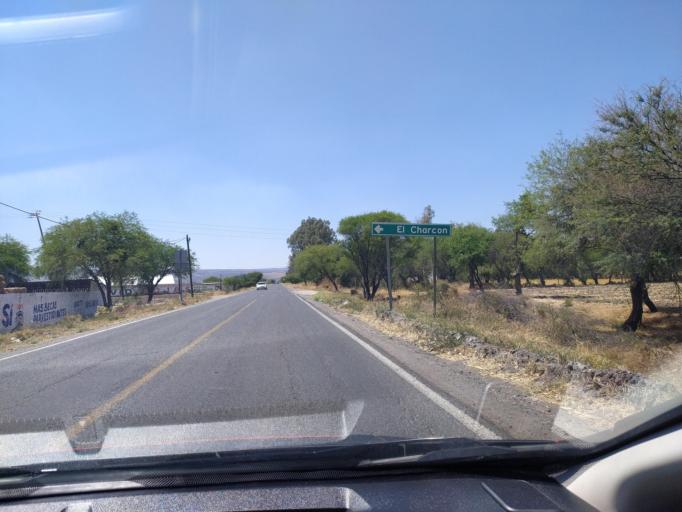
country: MX
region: Guanajuato
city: Ciudad Manuel Doblado
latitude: 20.7406
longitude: -101.9118
